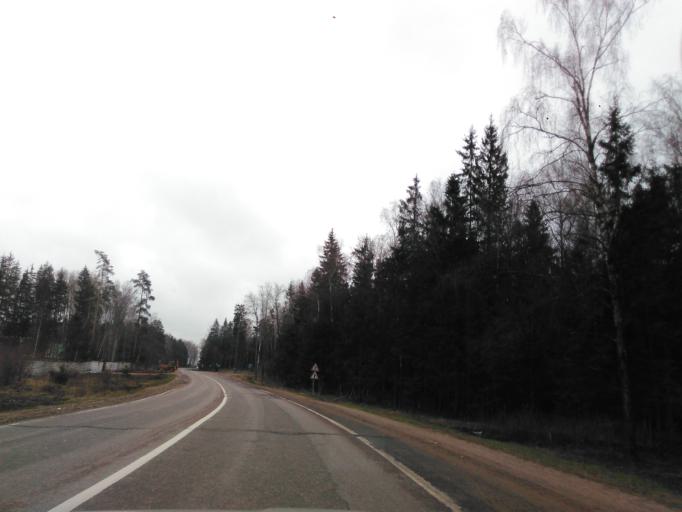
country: RU
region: Moskovskaya
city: Rozhdestveno
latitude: 55.8333
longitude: 37.0209
